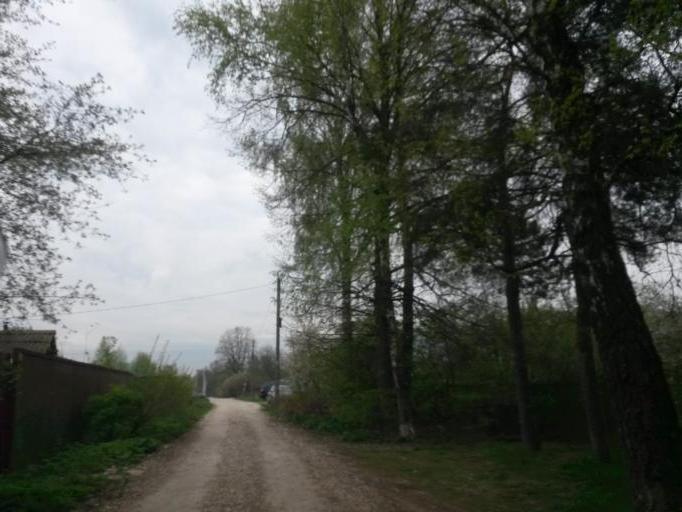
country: RU
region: Moskovskaya
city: Lyubuchany
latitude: 55.2536
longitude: 37.6076
